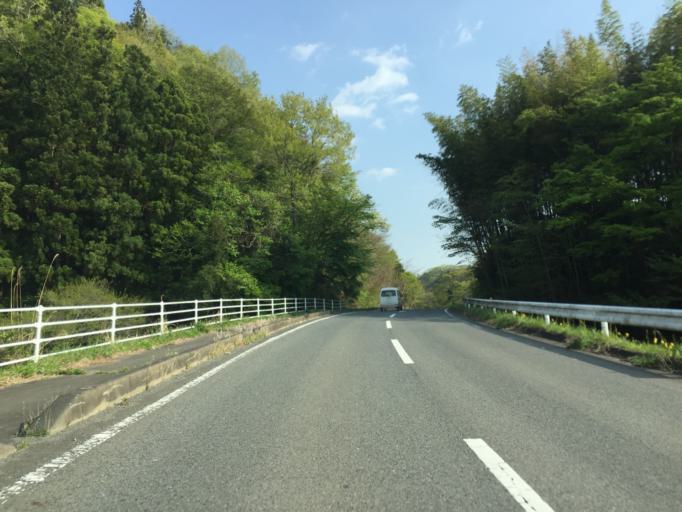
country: JP
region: Fukushima
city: Iwaki
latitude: 36.9985
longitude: 140.7894
